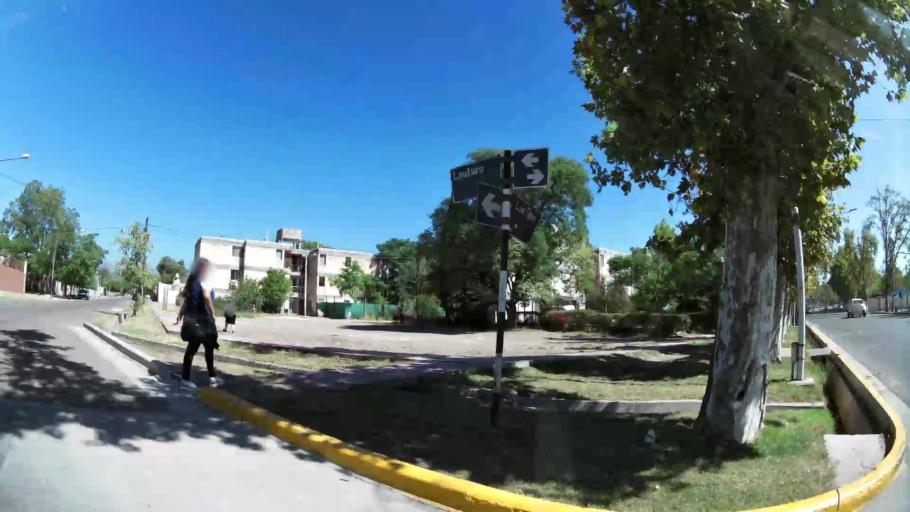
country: AR
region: Mendoza
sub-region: Departamento de Godoy Cruz
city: Godoy Cruz
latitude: -32.9056
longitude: -68.8669
